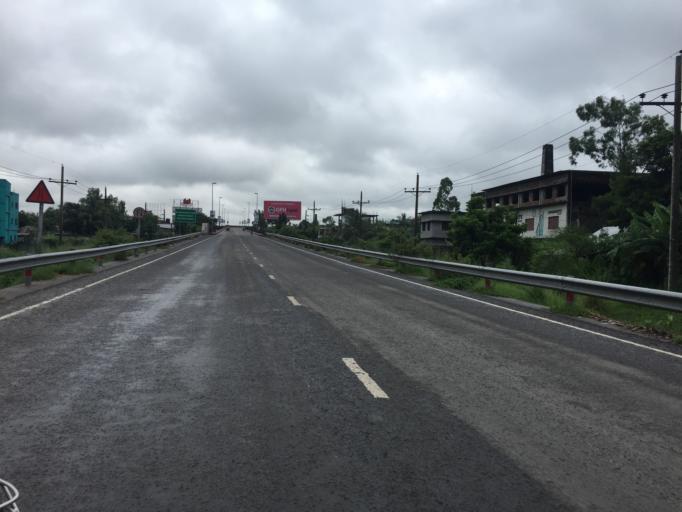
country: BD
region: Dhaka
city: Narayanganj
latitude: 23.5624
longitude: 90.5102
